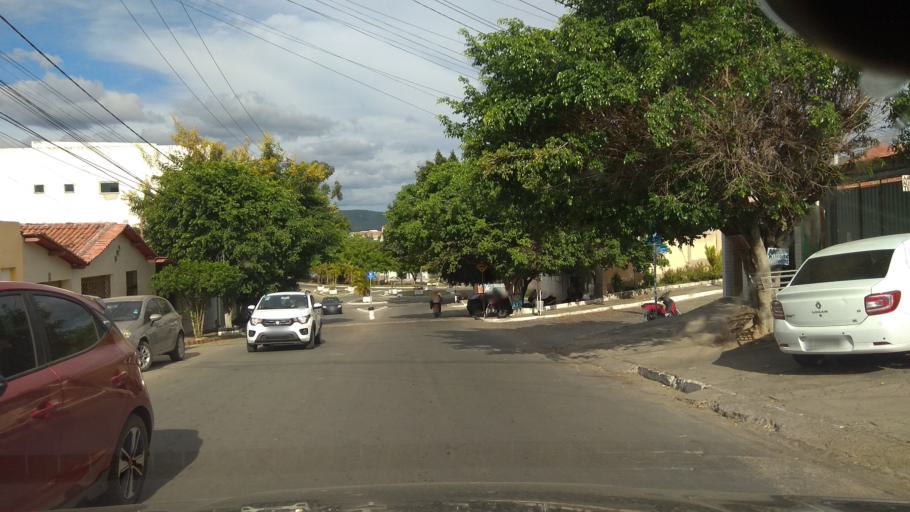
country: BR
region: Bahia
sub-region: Jequie
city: Jequie
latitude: -13.8711
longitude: -40.0703
